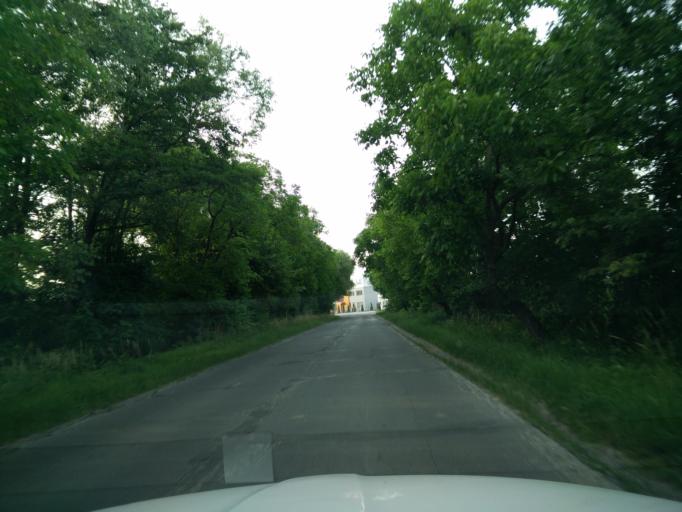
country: SK
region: Nitriansky
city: Prievidza
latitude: 48.7533
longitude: 18.6229
